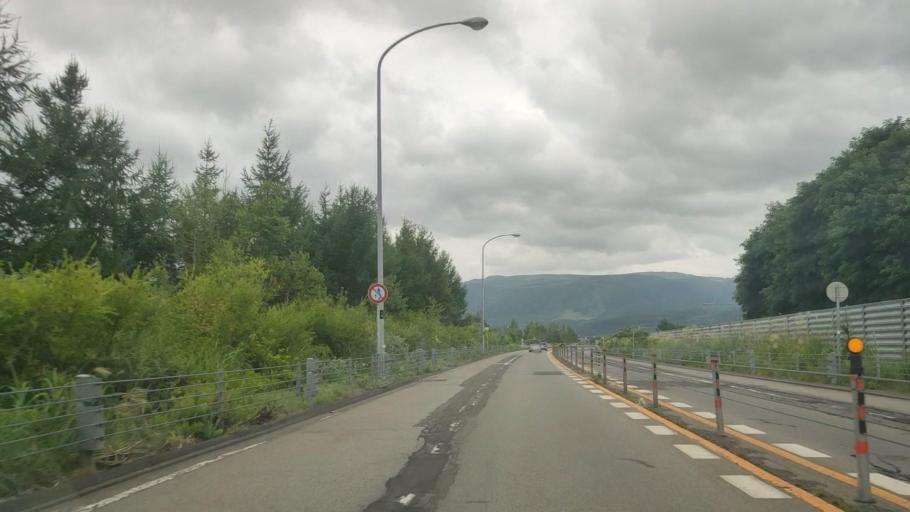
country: JP
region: Hokkaido
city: Nanae
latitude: 41.9156
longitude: 140.6869
